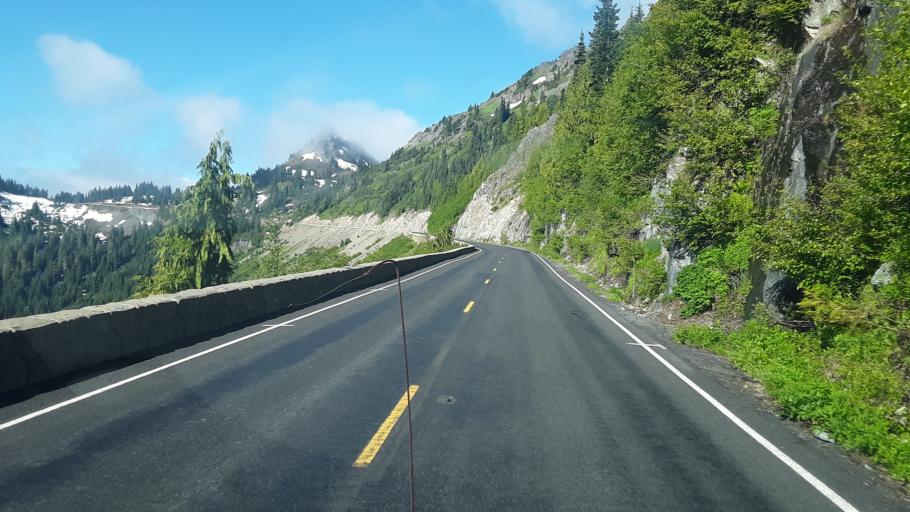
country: US
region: Washington
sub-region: King County
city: Enumclaw
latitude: 46.8856
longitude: -121.5064
